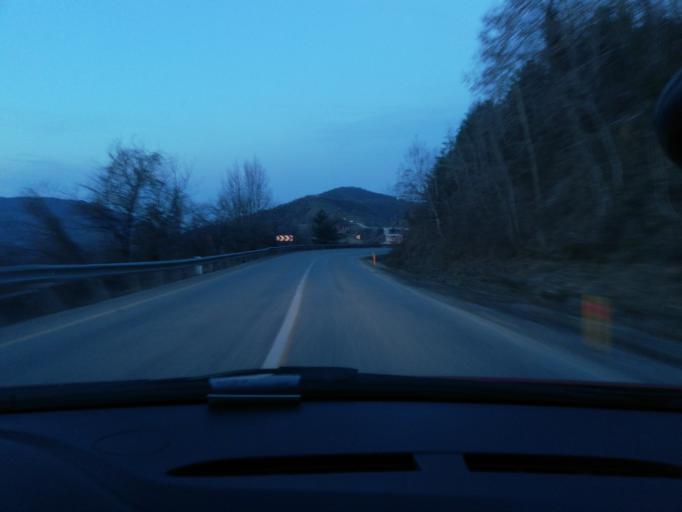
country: TR
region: Kastamonu
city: Inebolu
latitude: 41.9245
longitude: 33.7380
